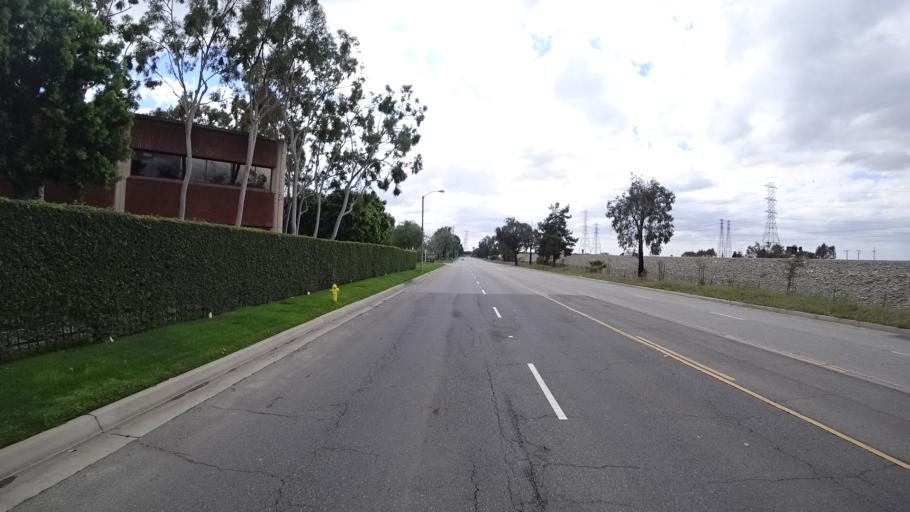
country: US
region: California
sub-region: Los Angeles County
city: Baldwin Park
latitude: 34.1017
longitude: -117.9806
